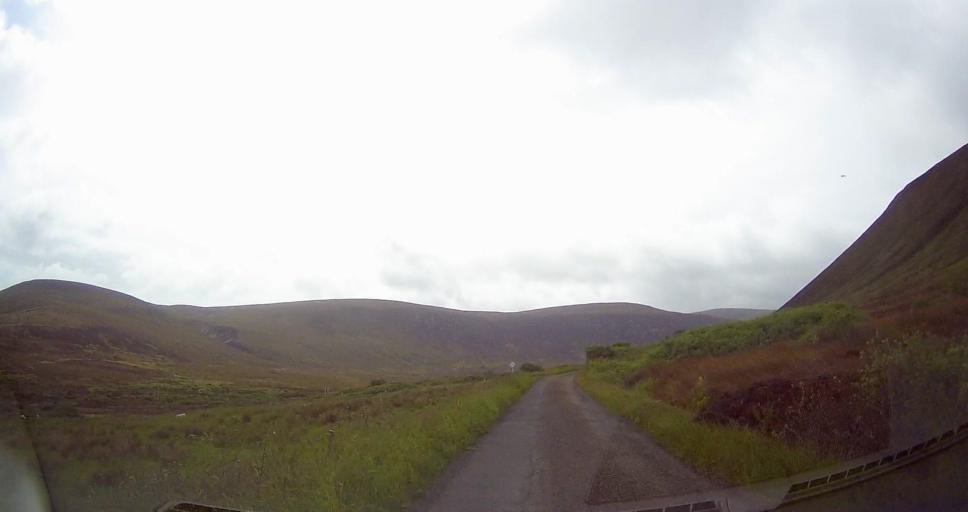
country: GB
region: Scotland
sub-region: Orkney Islands
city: Stromness
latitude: 58.9000
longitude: -3.3153
